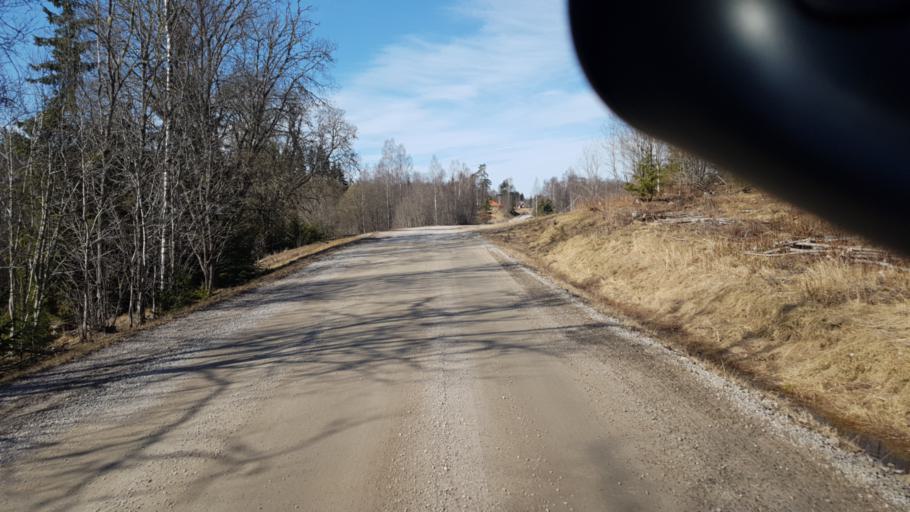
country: SE
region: Vaermland
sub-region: Sunne Kommun
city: Sunne
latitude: 59.6781
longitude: 12.8991
